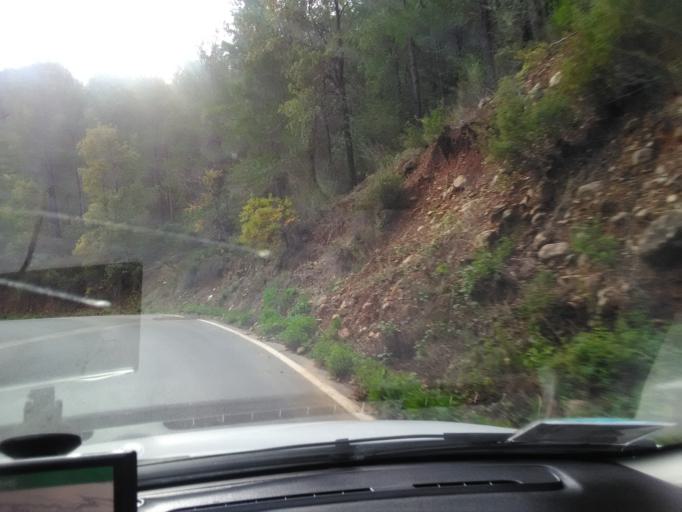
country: TR
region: Antalya
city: Gazipasa
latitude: 36.2554
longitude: 32.3931
